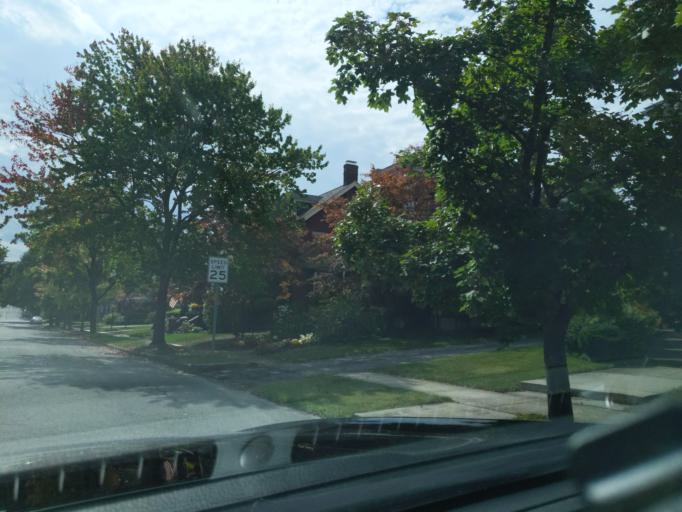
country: US
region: Pennsylvania
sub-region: Blair County
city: Hollidaysburg
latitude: 40.4345
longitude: -78.3905
